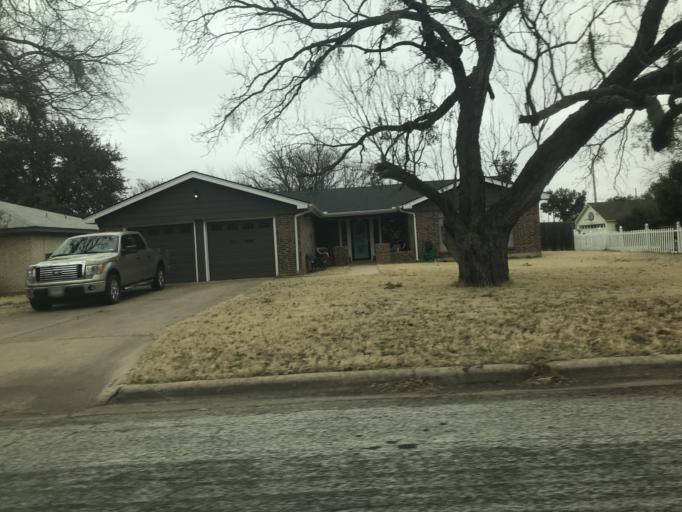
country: US
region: Texas
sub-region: Taylor County
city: Abilene
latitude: 32.4380
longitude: -99.7468
